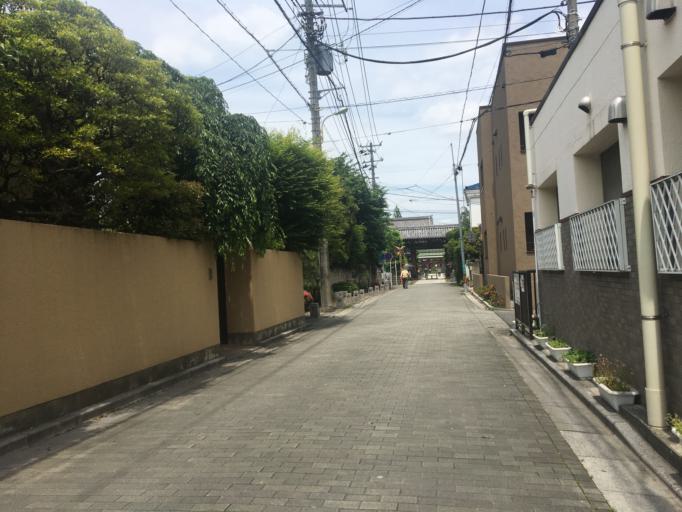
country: JP
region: Saitama
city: Shimotoda
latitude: 35.8268
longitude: 139.6775
